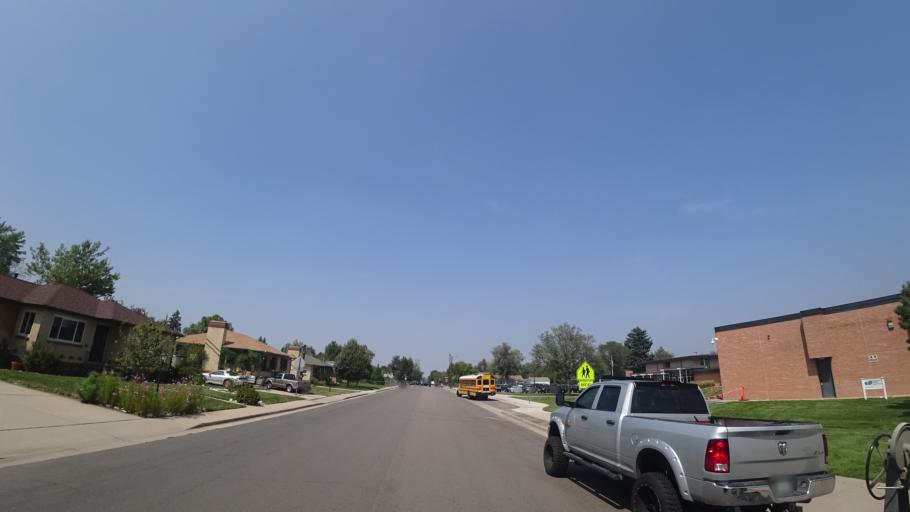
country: US
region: Colorado
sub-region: Arapahoe County
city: Englewood
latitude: 39.6266
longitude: -104.9926
